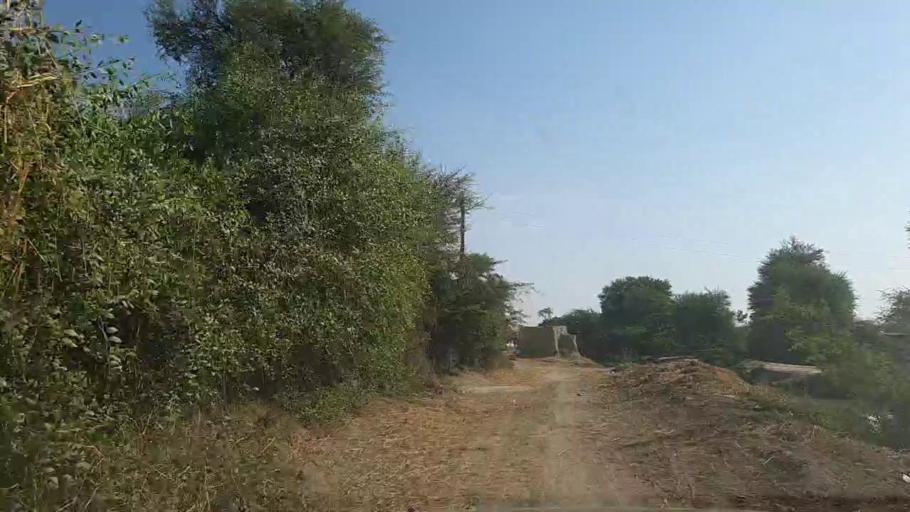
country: PK
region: Sindh
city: Bulri
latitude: 24.8577
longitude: 68.2884
